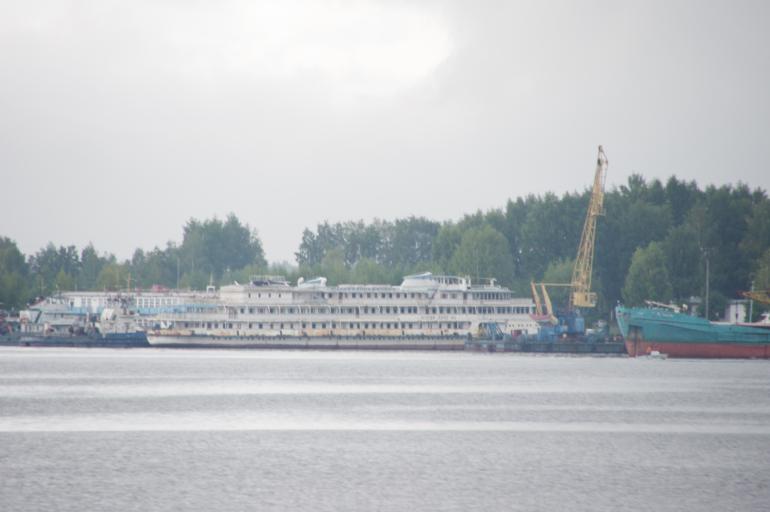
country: RU
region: Jaroslavl
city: Rybinsk
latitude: 58.1080
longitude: 38.6757
